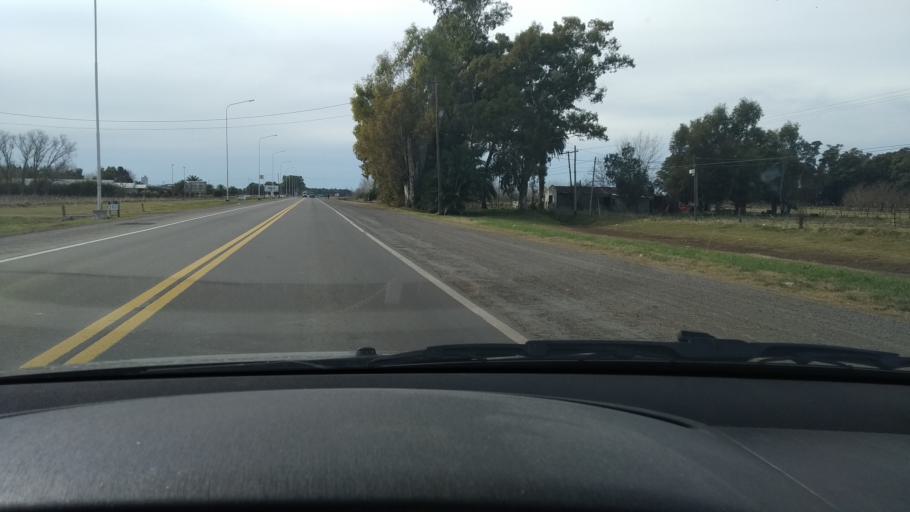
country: AR
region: Buenos Aires
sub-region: Partido de Azul
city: Azul
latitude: -36.7809
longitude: -59.8271
